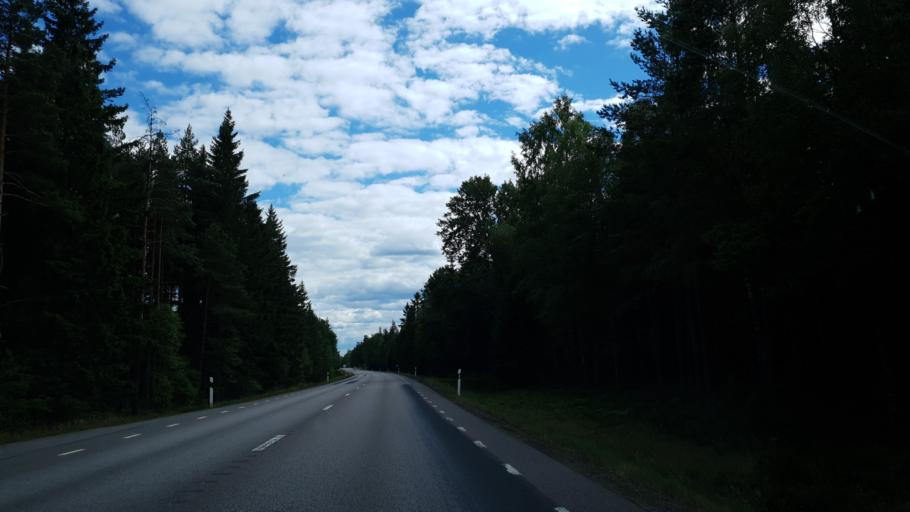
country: SE
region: Kronoberg
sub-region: Uppvidinge Kommun
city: Lenhovda
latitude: 56.8937
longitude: 15.3711
